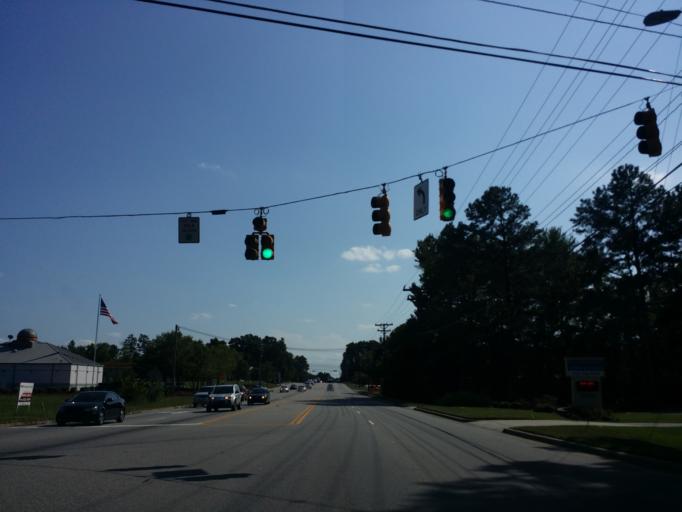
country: US
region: North Carolina
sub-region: Durham County
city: Durham
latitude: 35.9308
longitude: -78.8436
